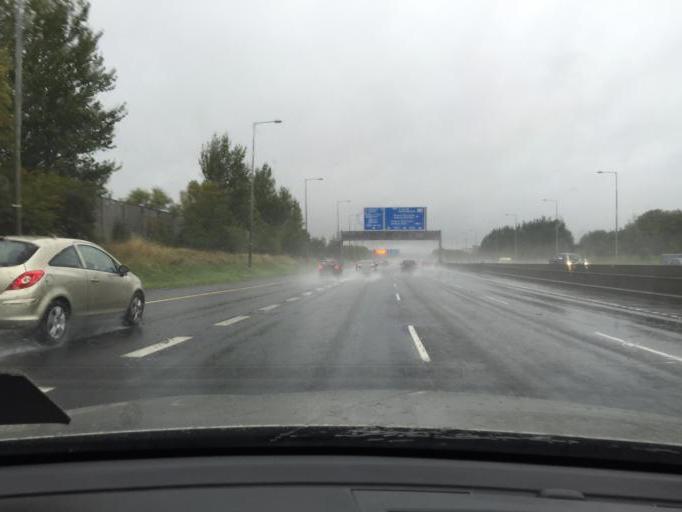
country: IE
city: Cherry Orchard
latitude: 53.3424
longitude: -6.3878
